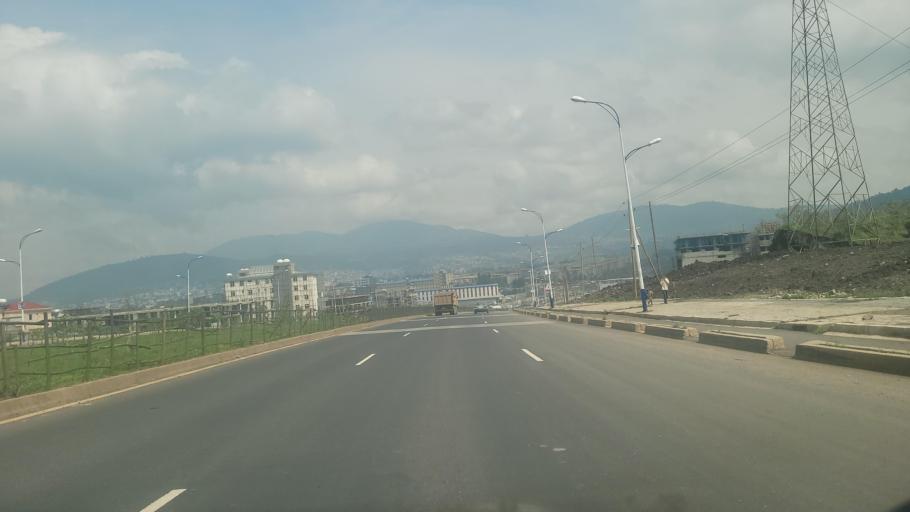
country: ET
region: Adis Abeba
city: Addis Ababa
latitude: 8.9510
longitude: 38.7022
